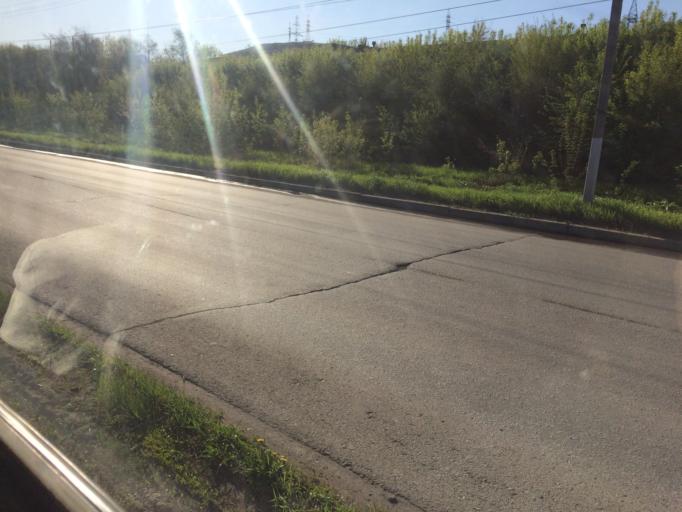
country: RU
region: Chelyabinsk
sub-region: Gorod Magnitogorsk
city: Magnitogorsk
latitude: 53.3969
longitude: 59.0311
